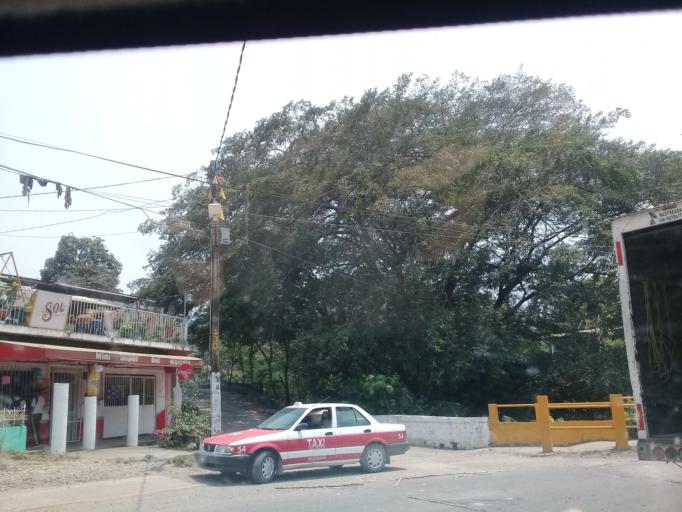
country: MX
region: Veracruz
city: Cosolapa
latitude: 18.5975
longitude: -96.6897
